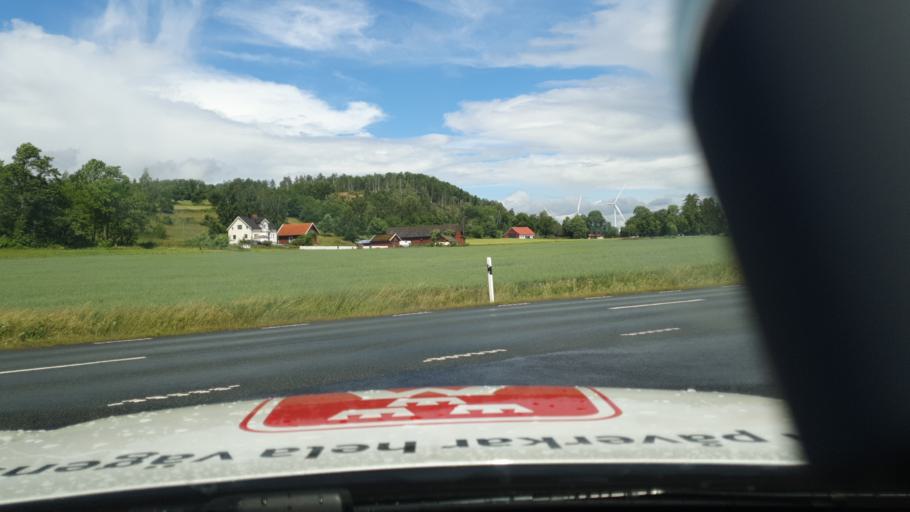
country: SE
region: Vaestra Goetaland
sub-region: Falkopings Kommun
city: Akarp
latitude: 58.1218
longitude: 13.7700
